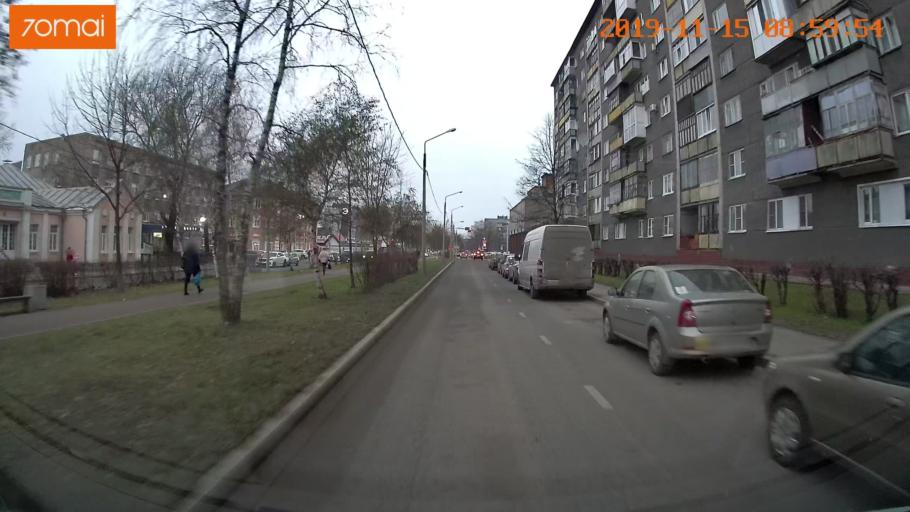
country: RU
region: Vologda
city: Cherepovets
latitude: 59.1286
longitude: 37.9242
